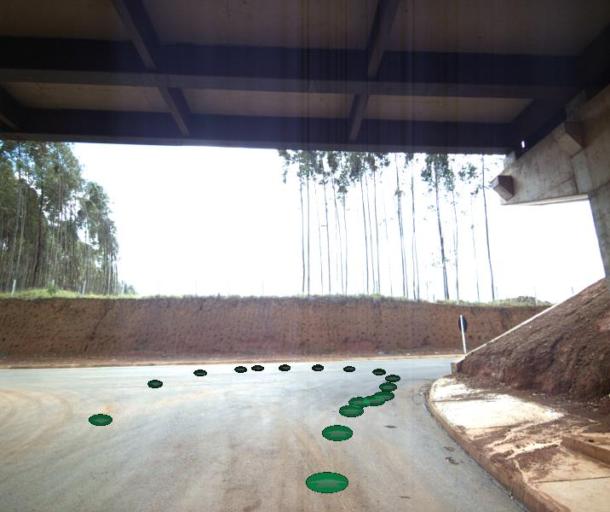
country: BR
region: Goias
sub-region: Anapolis
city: Anapolis
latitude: -16.2369
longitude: -49.0056
